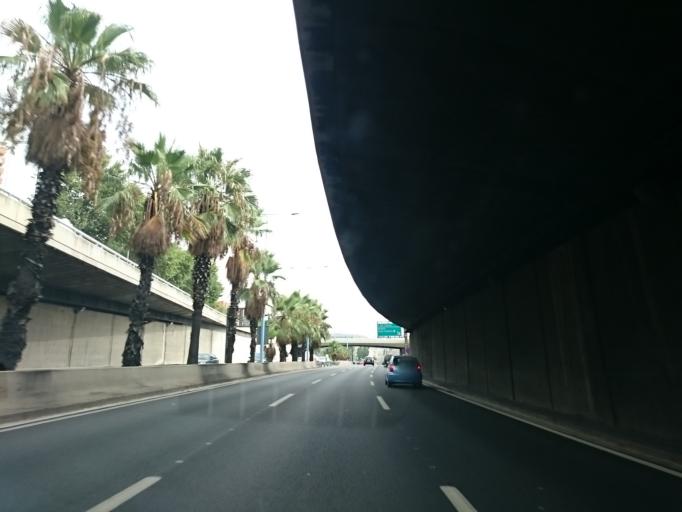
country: ES
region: Catalonia
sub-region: Provincia de Barcelona
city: Sarria-Sant Gervasi
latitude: 41.4234
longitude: 2.1415
